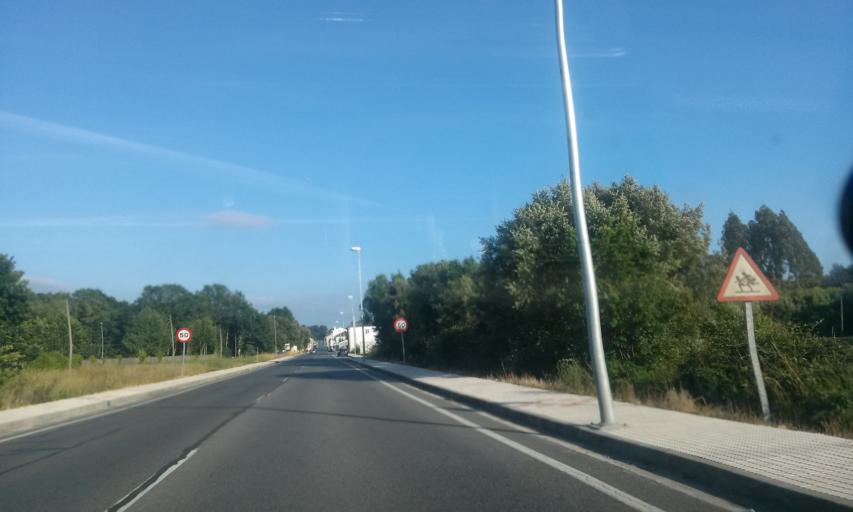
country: ES
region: Galicia
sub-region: Provincia de Lugo
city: Begonte
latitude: 43.1550
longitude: -7.6916
